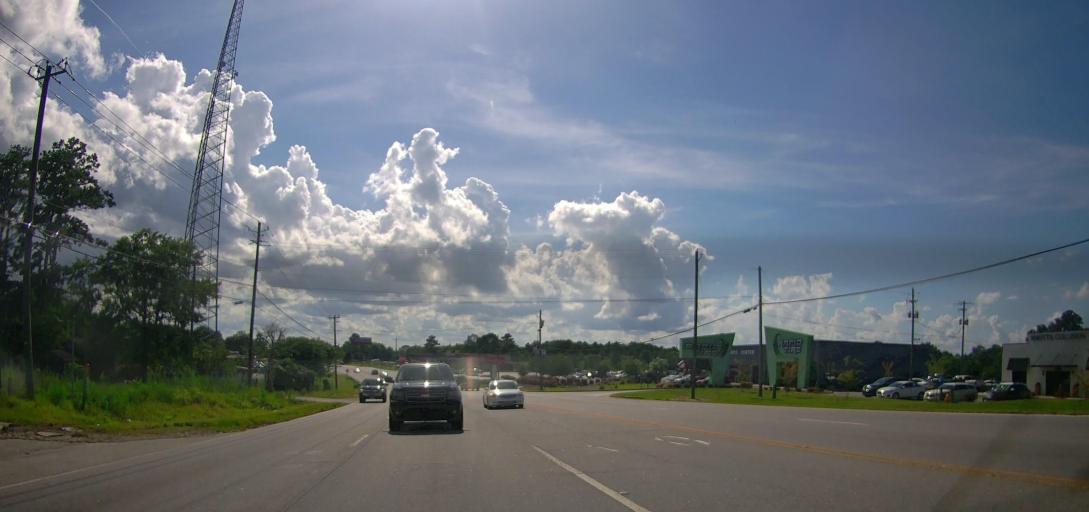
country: US
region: Alabama
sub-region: Russell County
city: Ladonia
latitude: 32.4704
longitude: -85.0964
